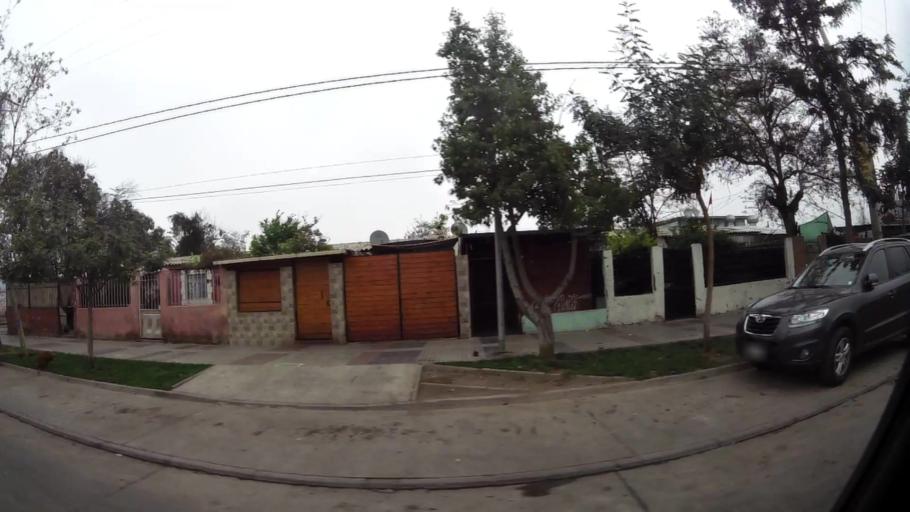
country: CL
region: Santiago Metropolitan
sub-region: Provincia de Santiago
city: Santiago
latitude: -33.4872
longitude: -70.6364
